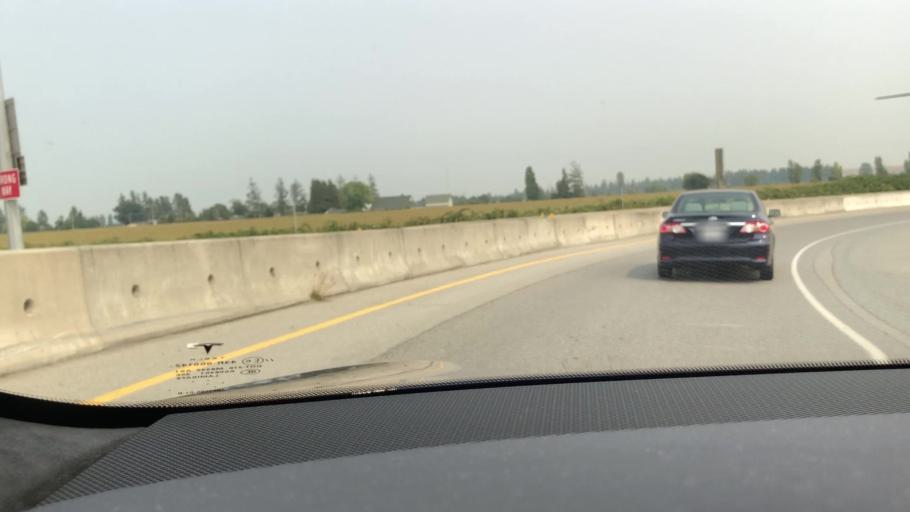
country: CA
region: British Columbia
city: Ladner
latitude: 49.1087
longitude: -123.0543
